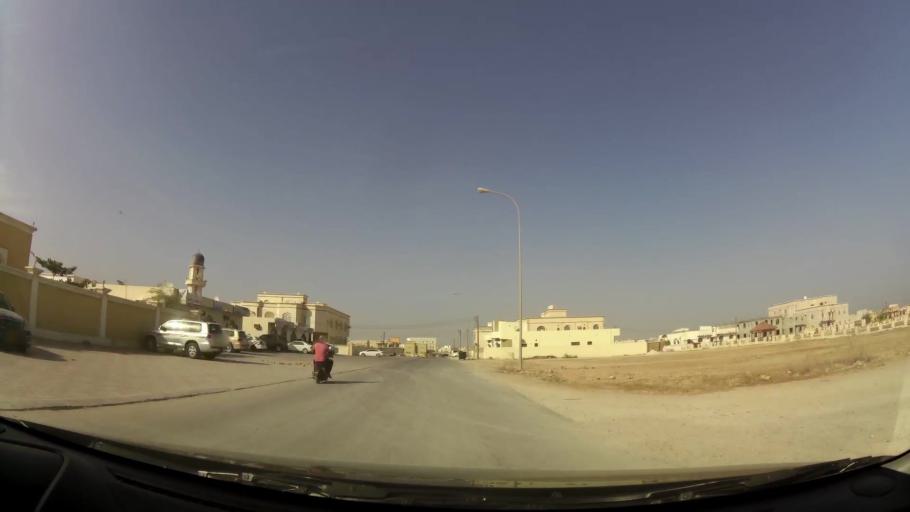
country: OM
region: Zufar
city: Salalah
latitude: 17.0051
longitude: 54.0219
